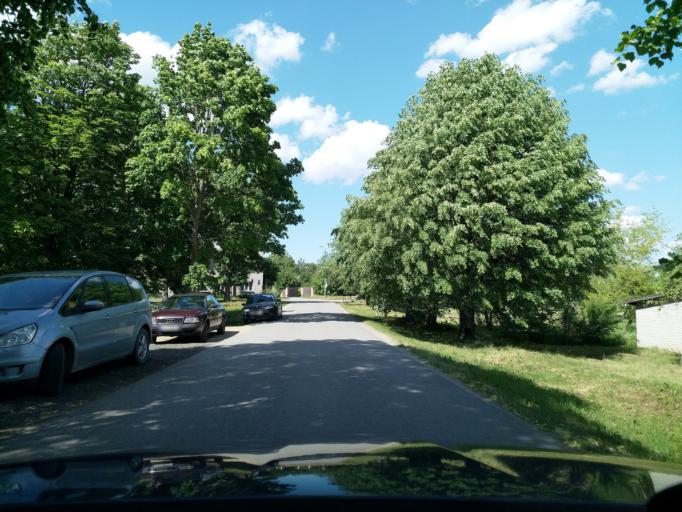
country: LV
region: Alsunga
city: Alsunga
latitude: 56.9779
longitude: 21.5654
